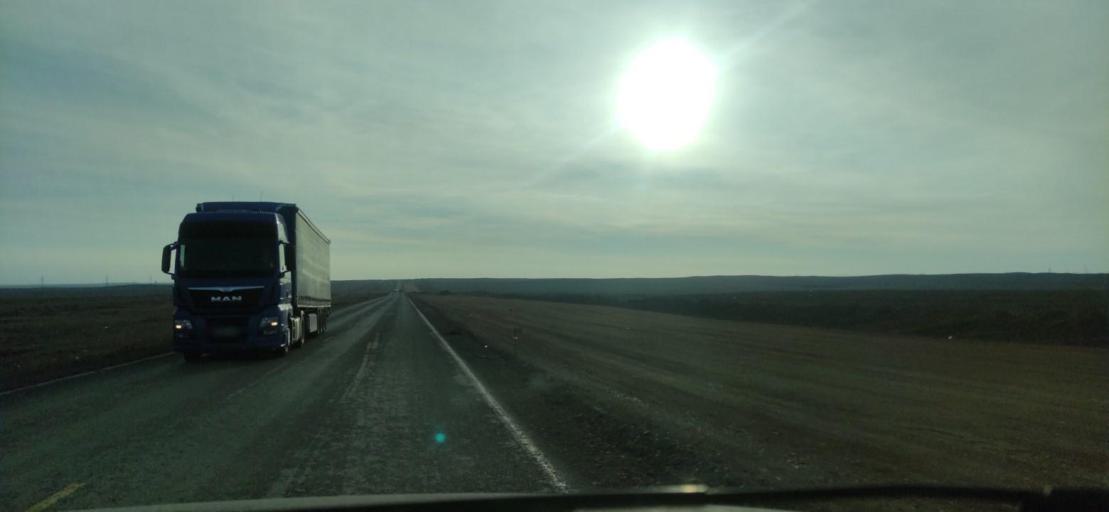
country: KZ
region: Qaraghandy
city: Saryshaghan
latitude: 46.1817
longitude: 73.6259
